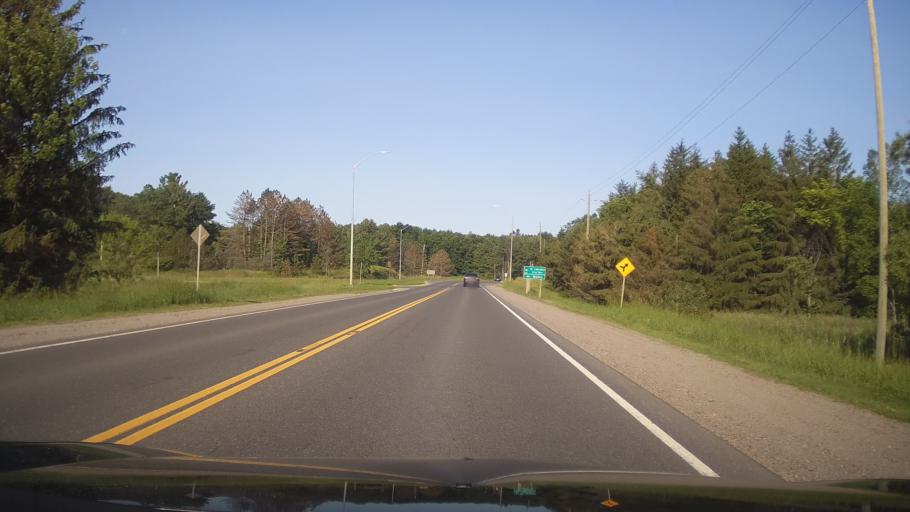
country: CA
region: Ontario
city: Quinte West
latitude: 44.5041
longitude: -77.4984
